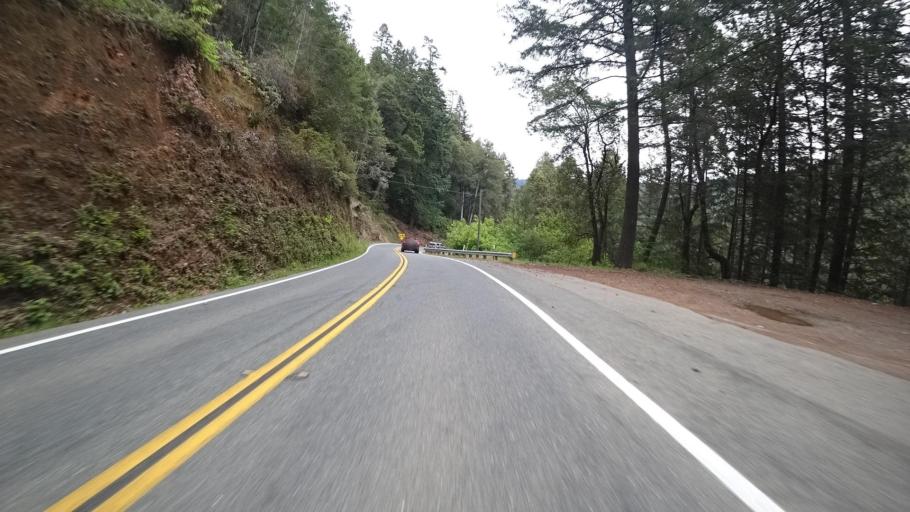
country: US
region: California
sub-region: Humboldt County
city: Willow Creek
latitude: 41.0113
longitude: -123.6369
